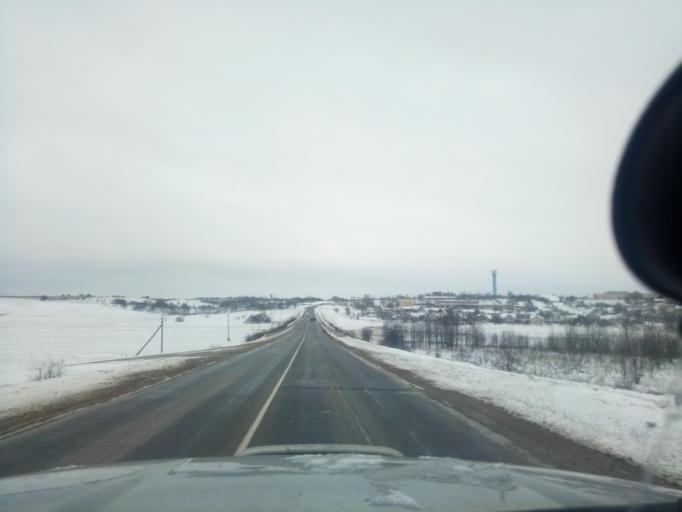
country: BY
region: Minsk
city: Kapyl'
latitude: 53.1422
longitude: 27.0817
